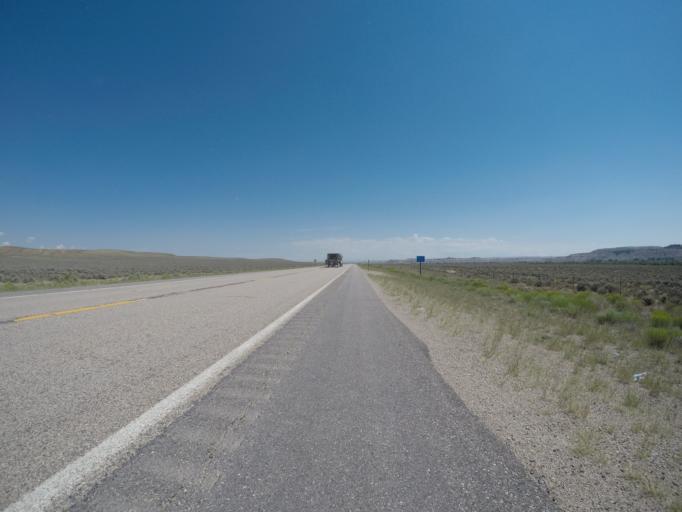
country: US
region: Wyoming
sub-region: Sublette County
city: Marbleton
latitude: 42.4309
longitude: -110.1062
